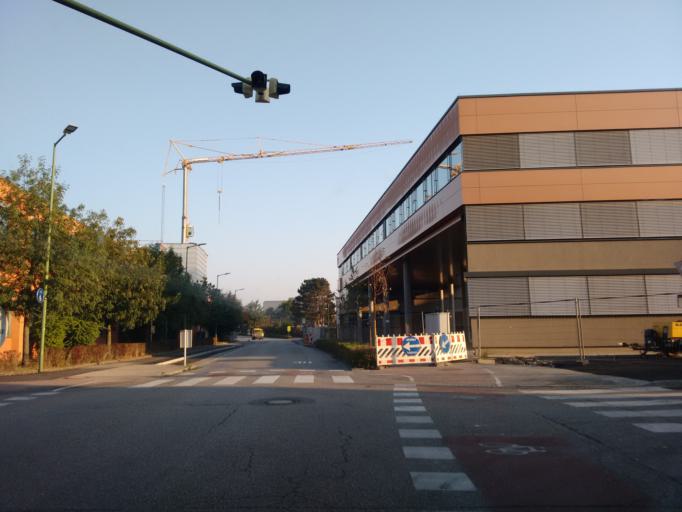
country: AT
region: Upper Austria
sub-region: Wels Stadt
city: Wels
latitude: 48.1697
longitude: 14.0215
